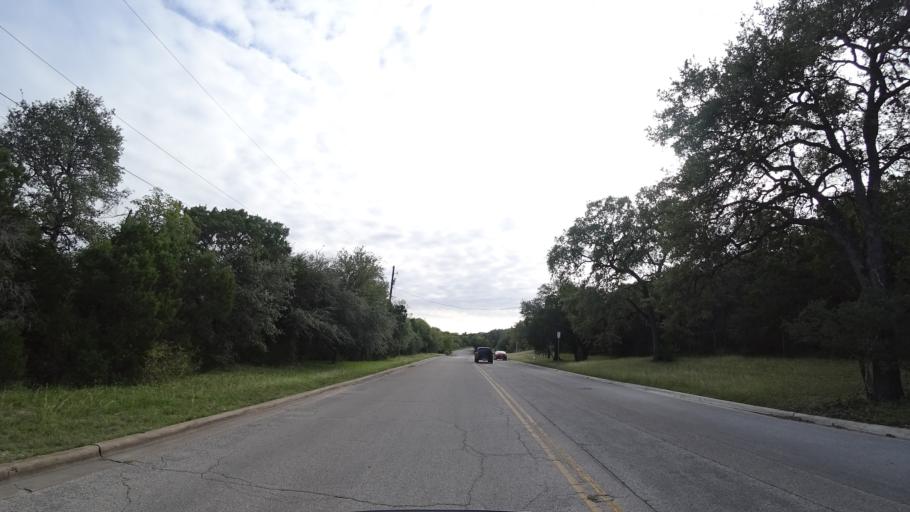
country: US
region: Texas
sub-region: Travis County
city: West Lake Hills
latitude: 30.2904
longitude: -97.7931
